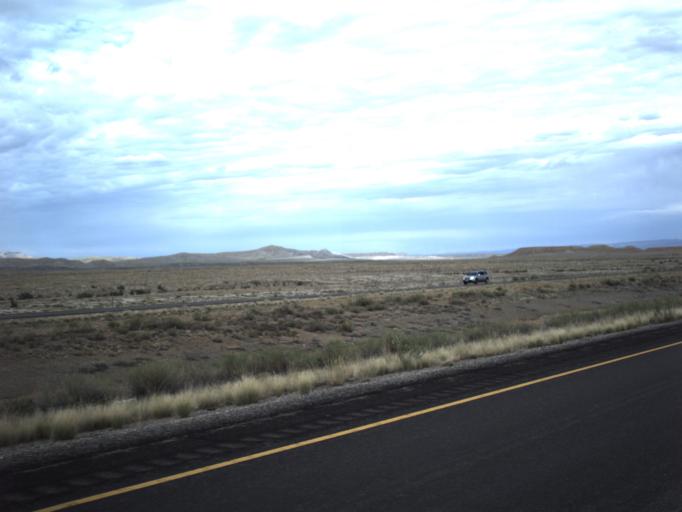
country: US
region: Utah
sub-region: Grand County
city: Moab
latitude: 38.9467
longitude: -109.6600
